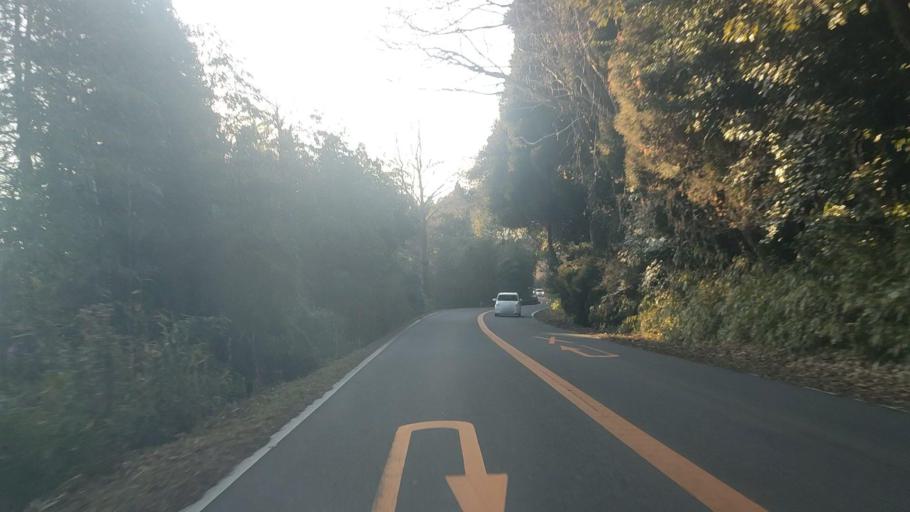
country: JP
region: Oita
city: Beppu
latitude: 33.2696
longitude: 131.4399
